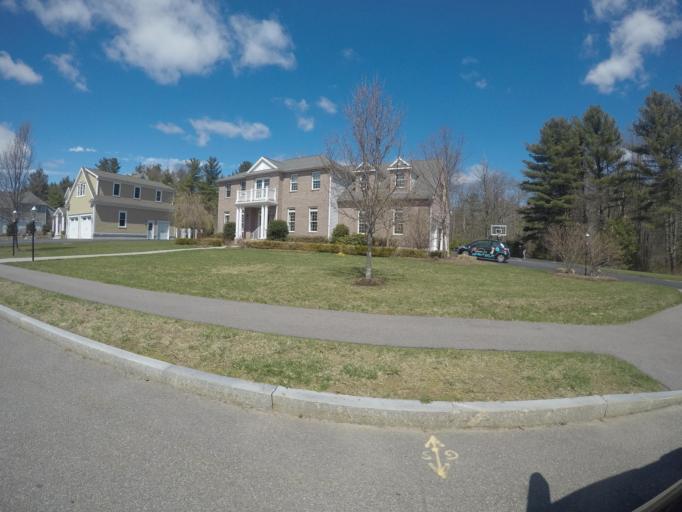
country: US
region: Massachusetts
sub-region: Bristol County
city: Easton
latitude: 42.0723
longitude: -71.1356
